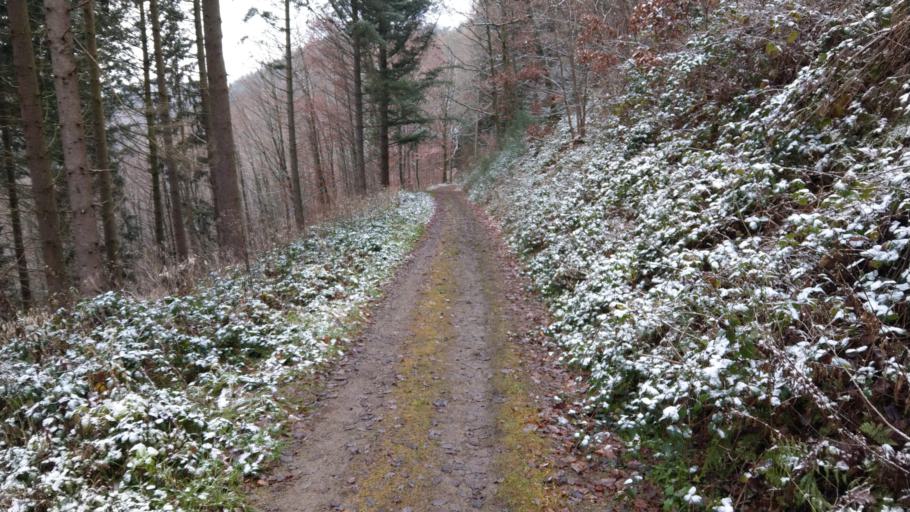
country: DE
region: North Rhine-Westphalia
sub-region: Regierungsbezirk Koln
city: Monschau
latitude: 50.5568
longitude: 6.2629
